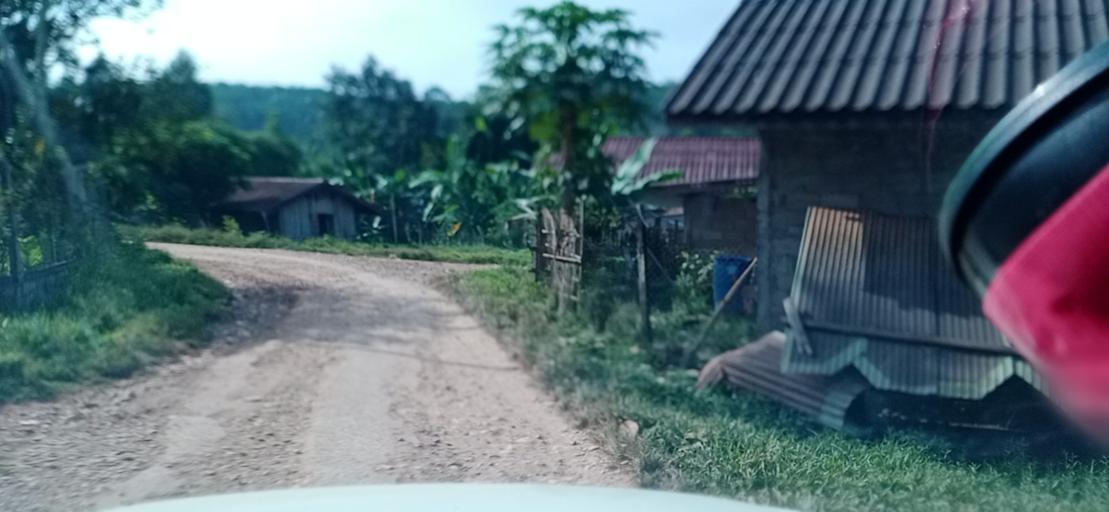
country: TH
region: Changwat Bueng Kan
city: Pak Khat
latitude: 18.6783
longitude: 103.1893
